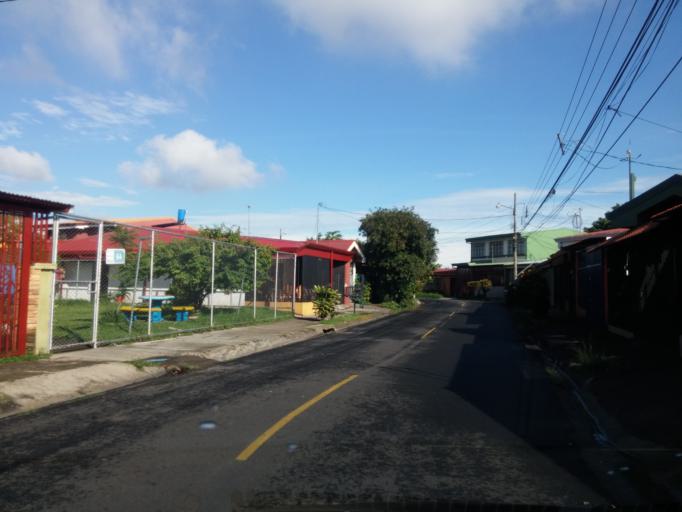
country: CR
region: Heredia
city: Mercedes
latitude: 10.0058
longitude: -84.1397
